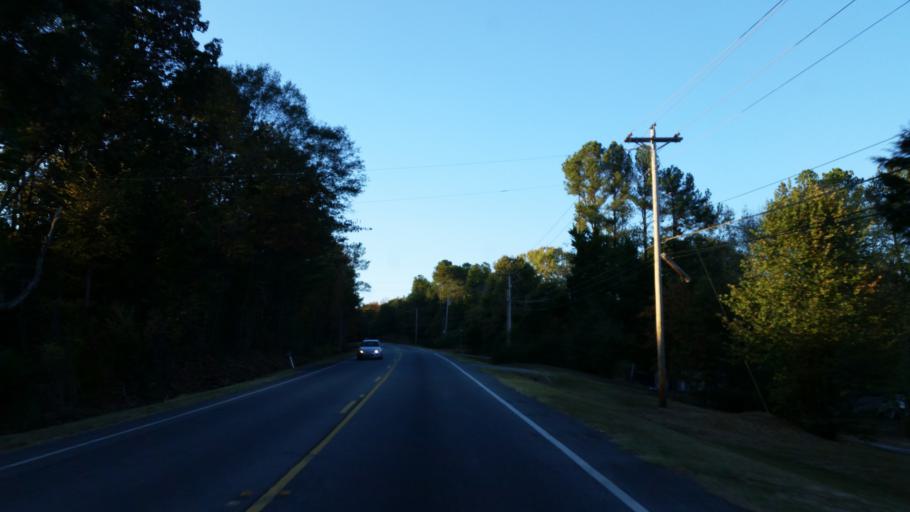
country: US
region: Georgia
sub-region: Gordon County
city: Calhoun
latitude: 34.5293
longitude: -84.9731
